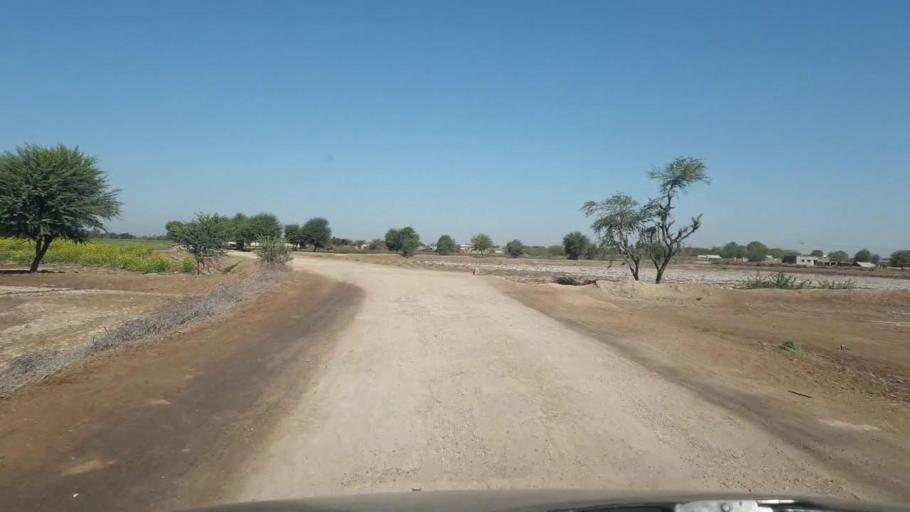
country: PK
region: Sindh
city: Umarkot
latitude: 25.3894
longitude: 69.6608
